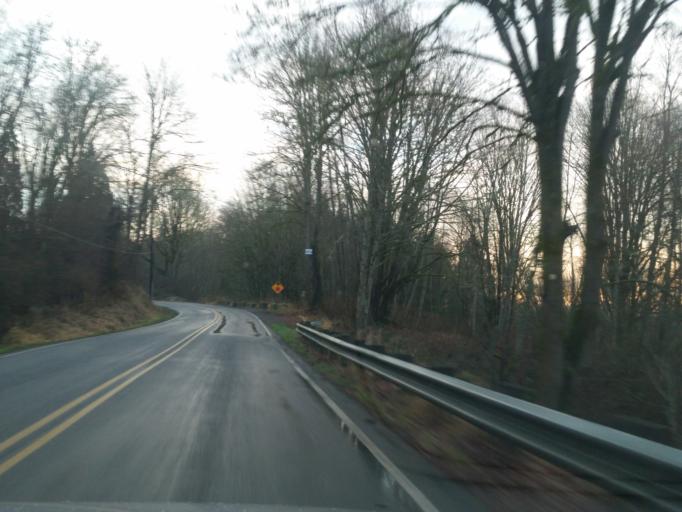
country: US
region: Washington
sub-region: Snohomish County
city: Cathcart
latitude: 47.8609
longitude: -122.0936
